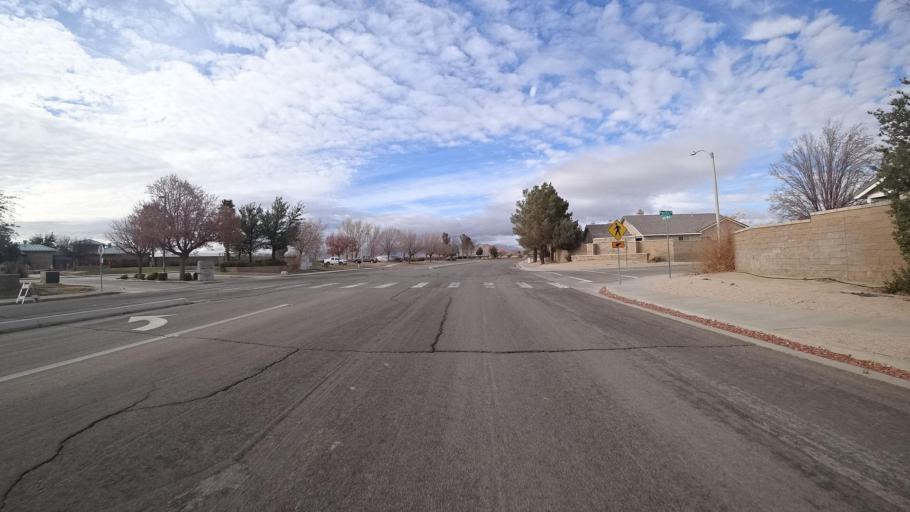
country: US
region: California
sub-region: Kern County
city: Rosamond
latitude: 34.8525
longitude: -118.2011
